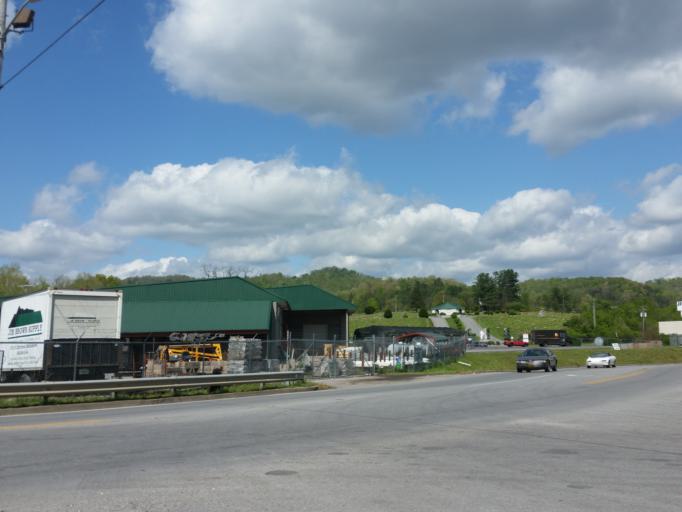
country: US
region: Kentucky
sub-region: Bell County
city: Middlesboro
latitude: 36.6230
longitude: -83.7087
